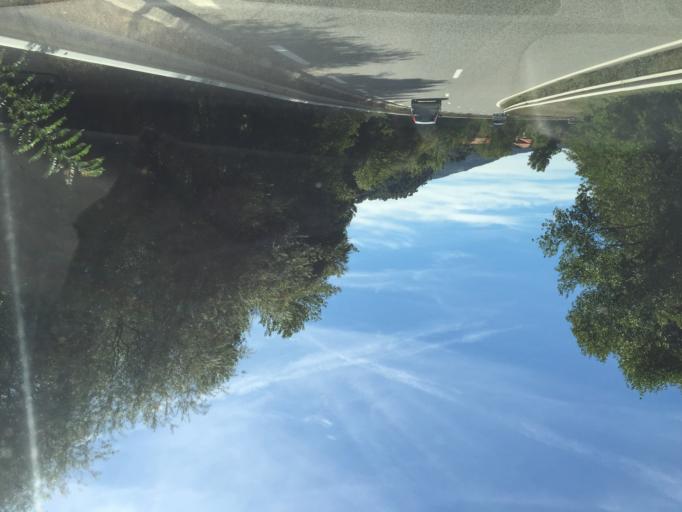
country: FR
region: Provence-Alpes-Cote d'Azur
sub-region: Departement des Alpes-Maritimes
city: Levens
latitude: 43.8581
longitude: 7.1962
